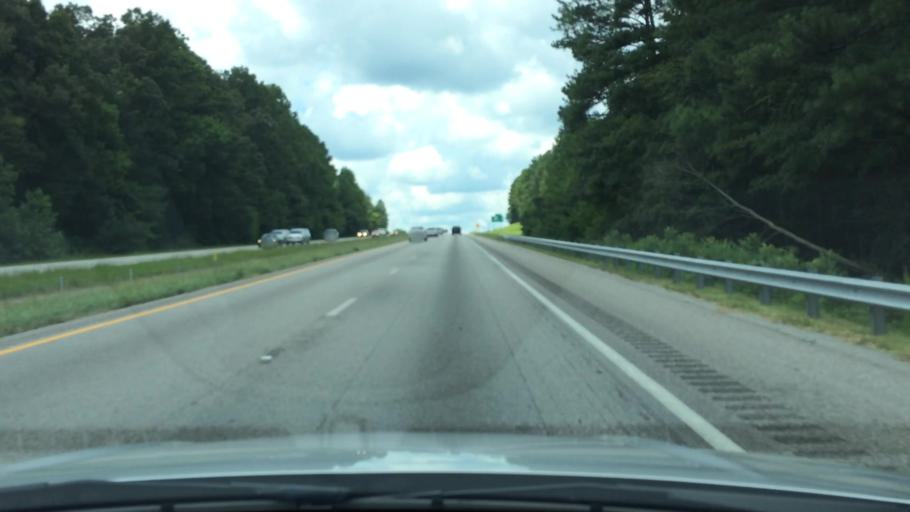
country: US
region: South Carolina
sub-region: Laurens County
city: Clinton
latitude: 34.4925
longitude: -81.8392
